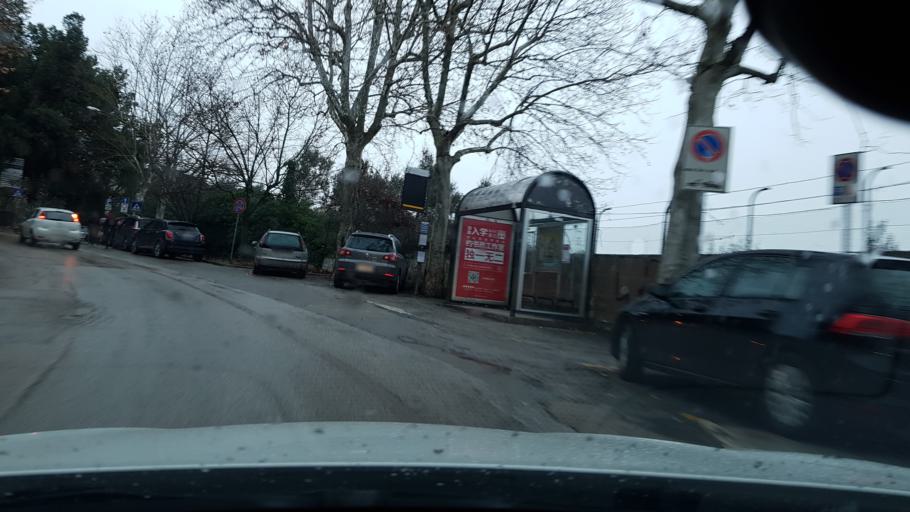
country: IT
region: Umbria
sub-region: Provincia di Perugia
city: Perugia
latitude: 43.1121
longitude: 12.3942
